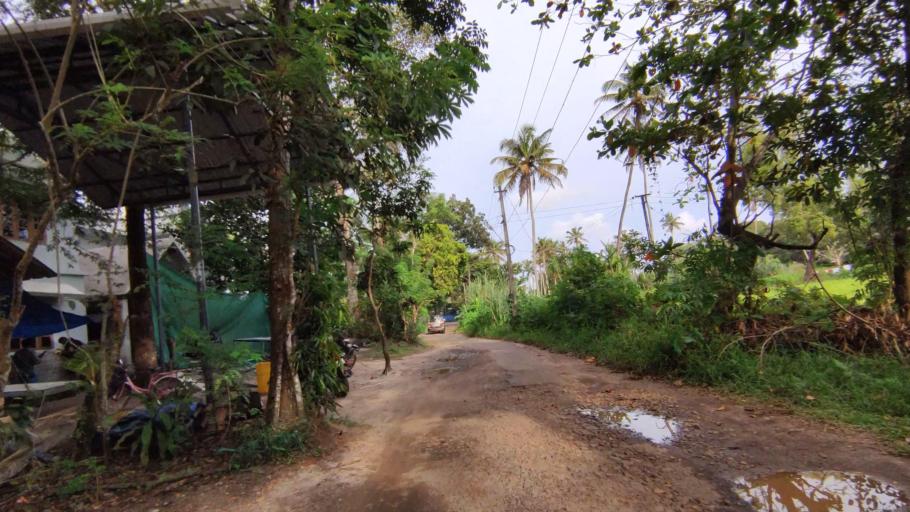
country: IN
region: Kerala
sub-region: Alappuzha
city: Shertallai
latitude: 9.6247
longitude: 76.3329
